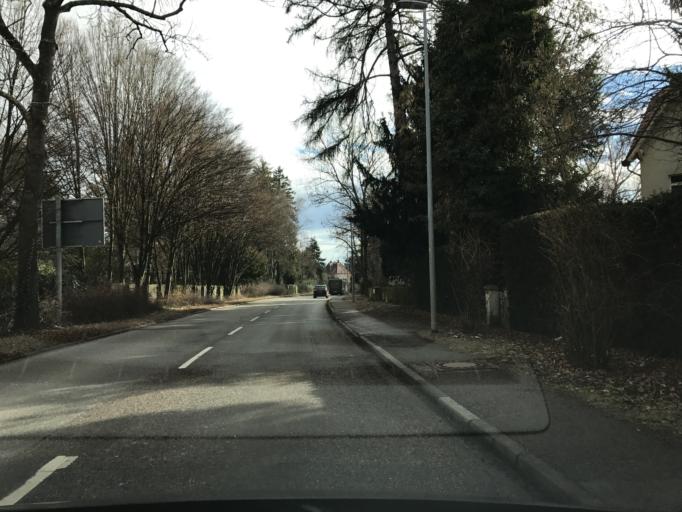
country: DE
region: Baden-Wuerttemberg
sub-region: Regierungsbezirk Stuttgart
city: Leinfelden-Echterdingen
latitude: 48.7099
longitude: 9.2041
